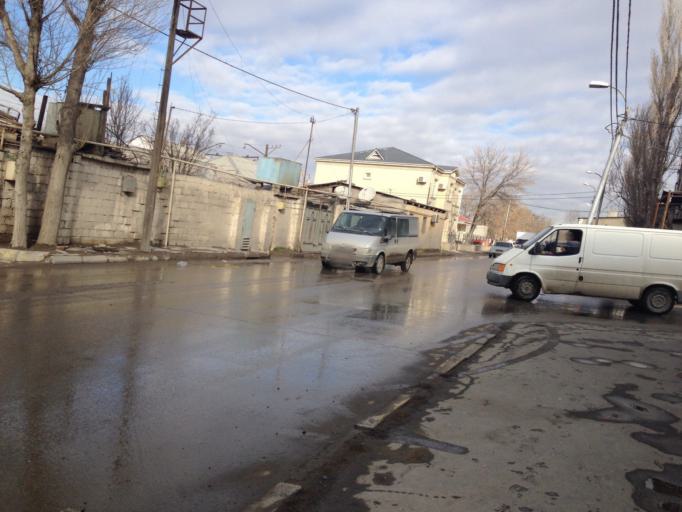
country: AZ
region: Baki
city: Baku
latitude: 40.3956
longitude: 49.8903
